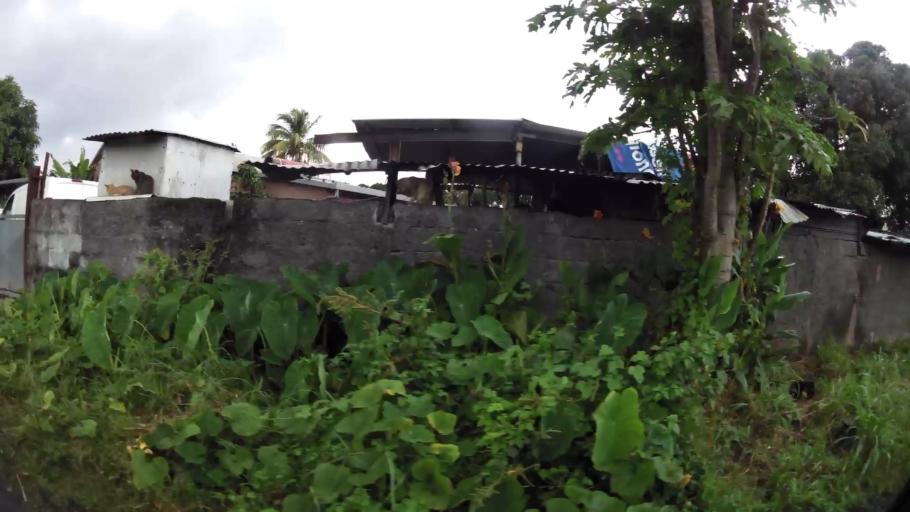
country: RE
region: Reunion
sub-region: Reunion
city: Saint-Andre
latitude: -20.9283
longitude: 55.6431
